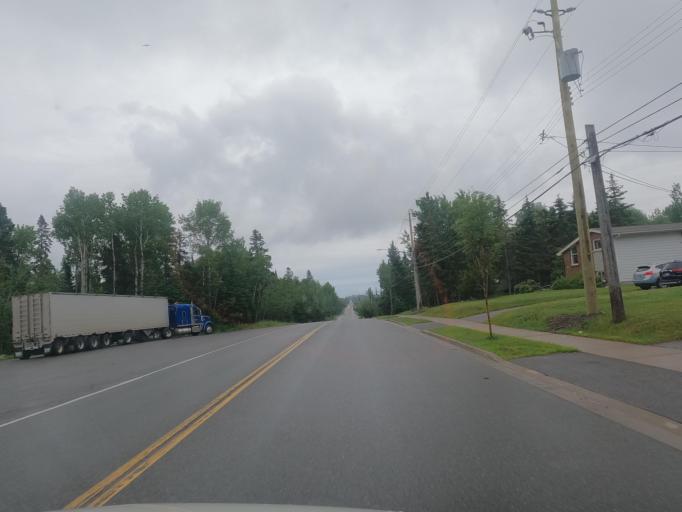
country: CA
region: Ontario
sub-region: Thunder Bay District
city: Thunder Bay
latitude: 48.4810
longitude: -89.1823
